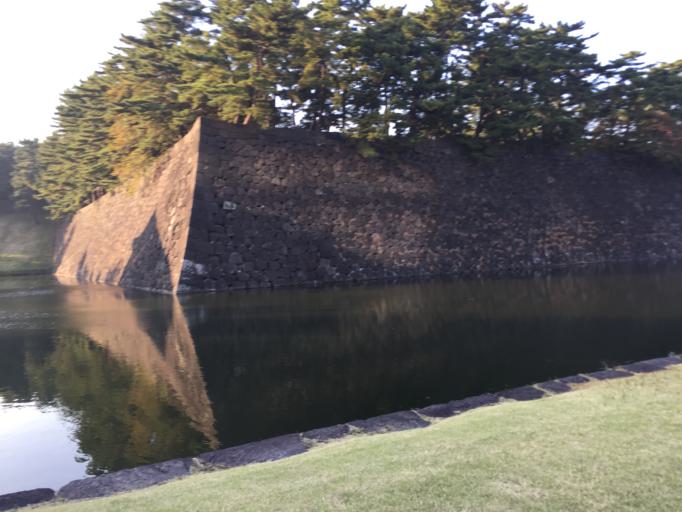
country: JP
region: Tokyo
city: Tokyo
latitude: 35.6785
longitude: 139.7549
